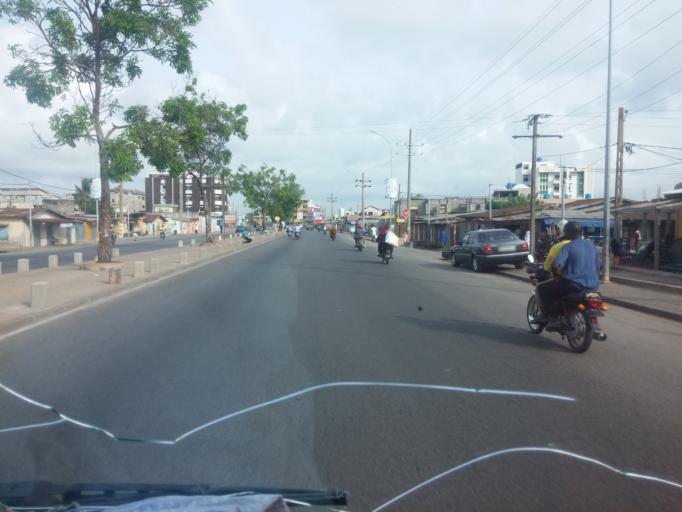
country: BJ
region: Littoral
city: Cotonou
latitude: 6.3736
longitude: 2.4074
